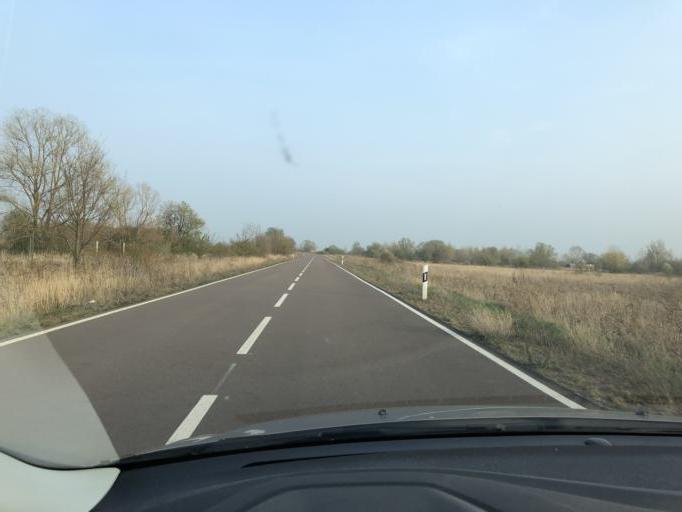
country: DE
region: Saxony
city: Dobernitz
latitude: 51.5009
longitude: 12.3147
